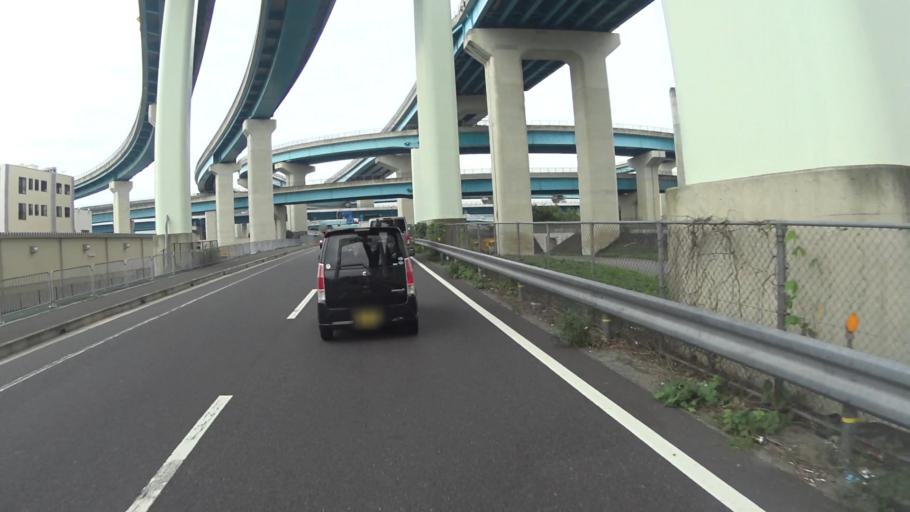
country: JP
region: Kyoto
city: Yawata
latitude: 34.8974
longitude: 135.7472
